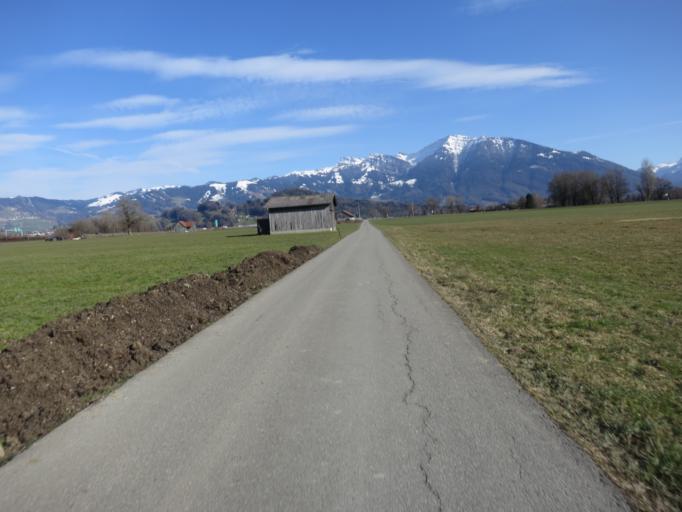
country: CH
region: Schwyz
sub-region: Bezirk March
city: Reichenburg
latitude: 47.1788
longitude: 8.9710
